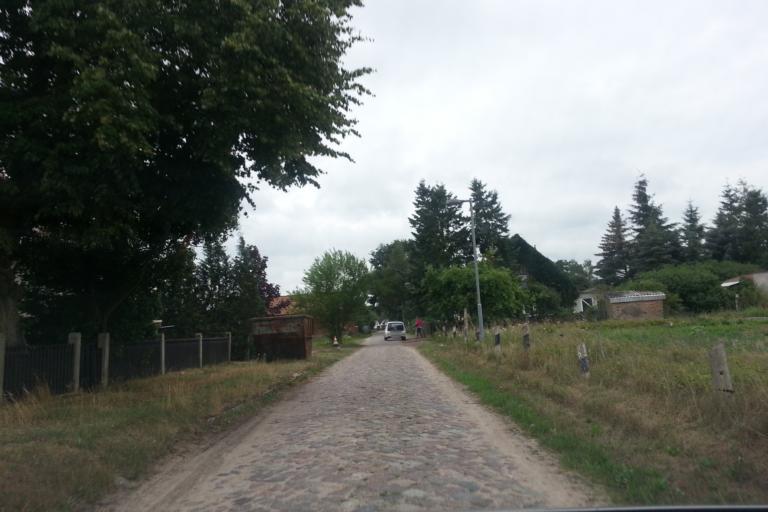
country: DE
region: Mecklenburg-Vorpommern
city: Ferdinandshof
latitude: 53.6956
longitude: 13.8957
